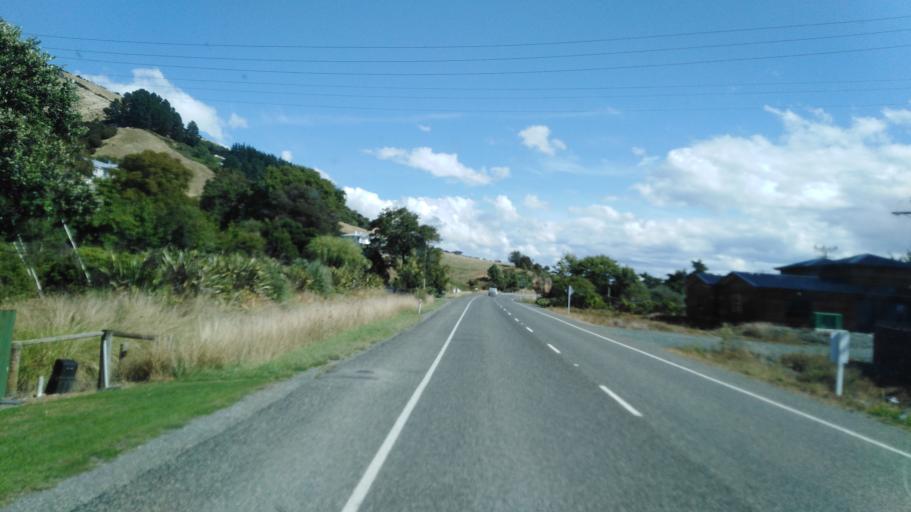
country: NZ
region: Nelson
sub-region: Nelson City
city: Nelson
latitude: -41.2190
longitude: 173.3296
